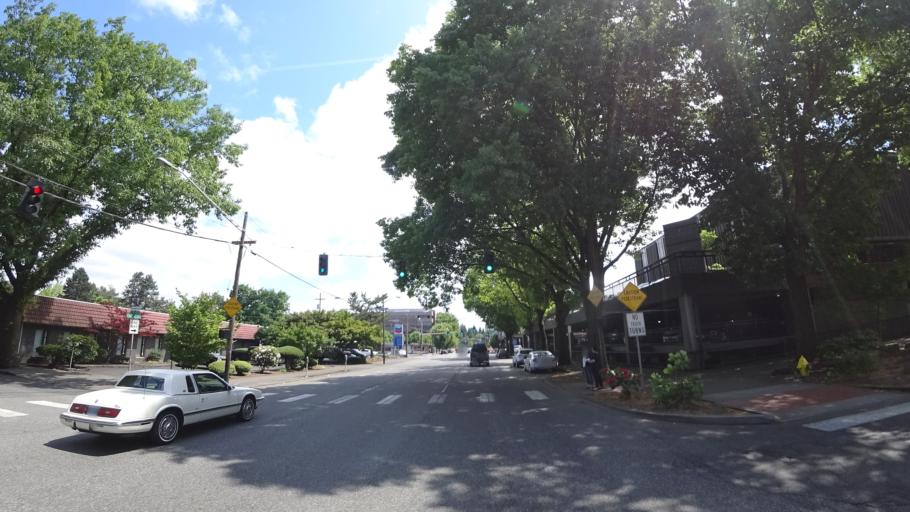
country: US
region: Washington
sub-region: Clark County
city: Vancouver
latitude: 45.6318
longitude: -122.6706
